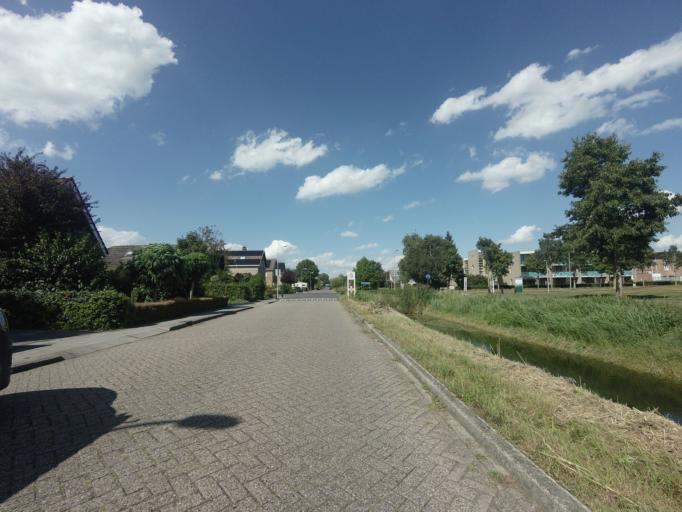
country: NL
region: Drenthe
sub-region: Gemeente Hoogeveen
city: Hoogeveen
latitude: 52.5950
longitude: 6.4602
